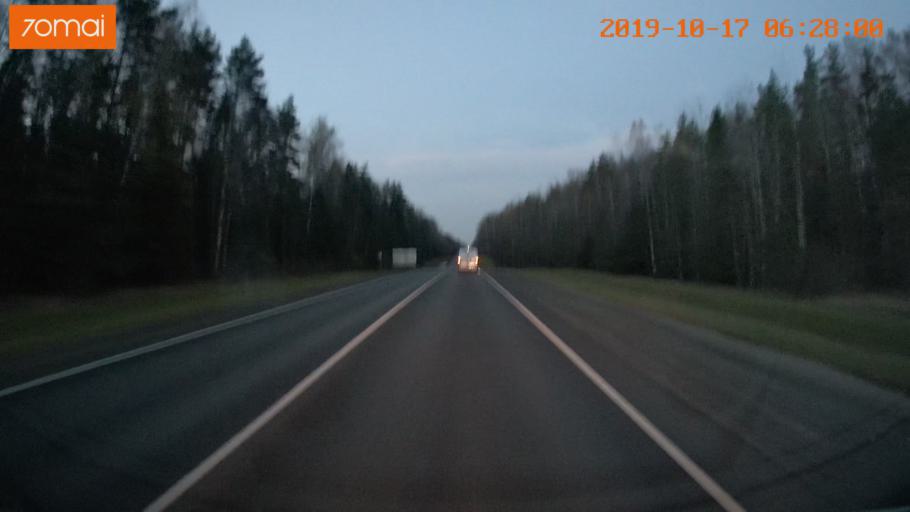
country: RU
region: Ivanovo
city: Lezhnevo
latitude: 56.7566
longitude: 40.7735
